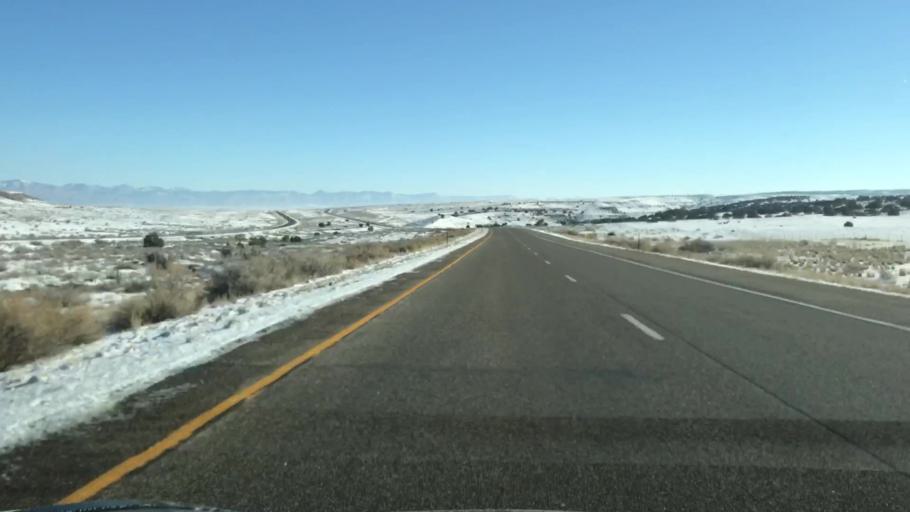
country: US
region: Colorado
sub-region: Mesa County
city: Loma
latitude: 39.2213
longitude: -108.9524
